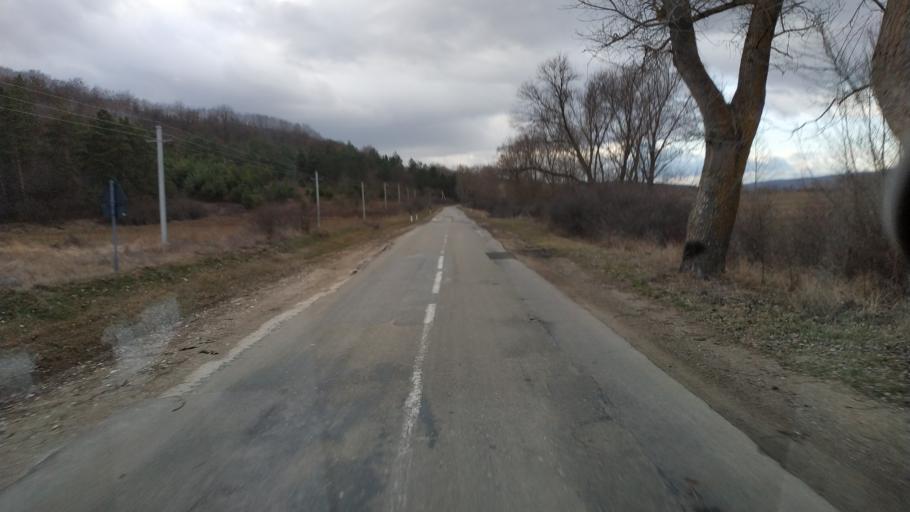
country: MD
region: Calarasi
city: Calarasi
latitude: 47.3138
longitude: 28.3389
